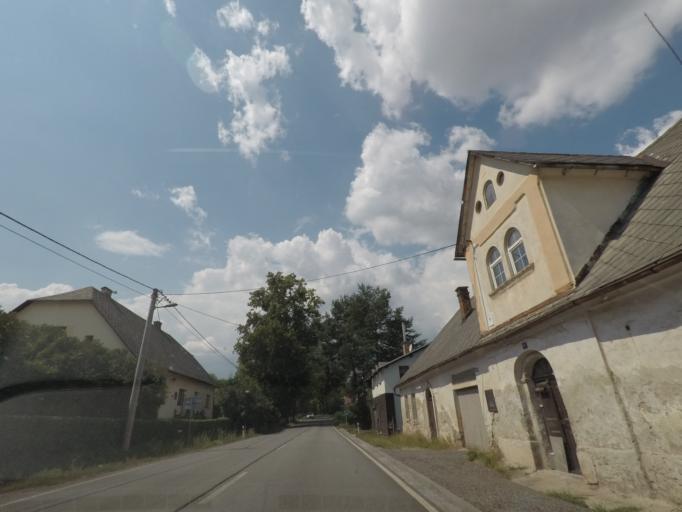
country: CZ
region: Kralovehradecky
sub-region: Okres Jicin
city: Pecka
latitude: 50.5389
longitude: 15.6391
